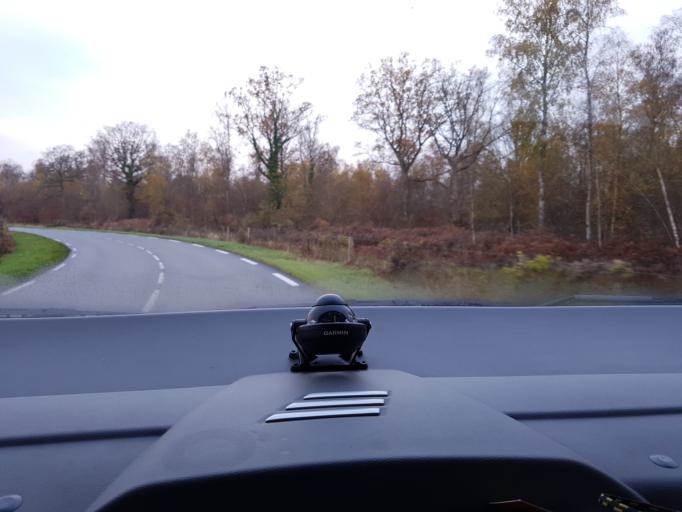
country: FR
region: Haute-Normandie
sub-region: Departement de la Seine-Maritime
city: Duclair
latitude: 49.4935
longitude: 0.8988
